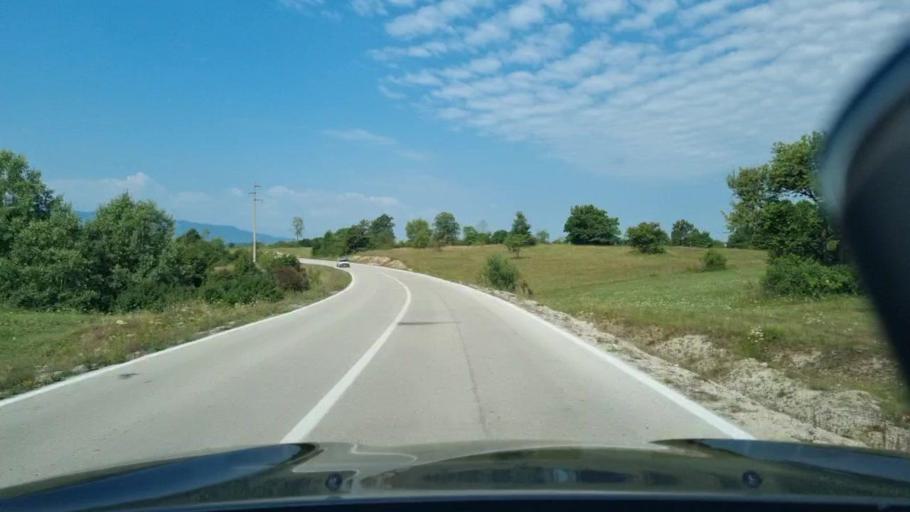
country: BA
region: Federation of Bosnia and Herzegovina
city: Ostrozac
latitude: 44.8854
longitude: 15.9289
